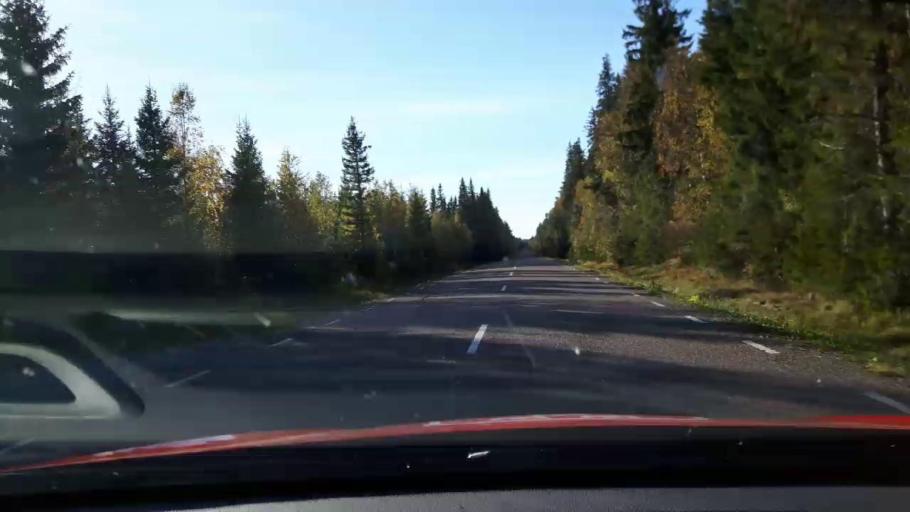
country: SE
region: Jaemtland
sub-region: Stroemsunds Kommun
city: Stroemsund
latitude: 63.8470
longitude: 15.2872
